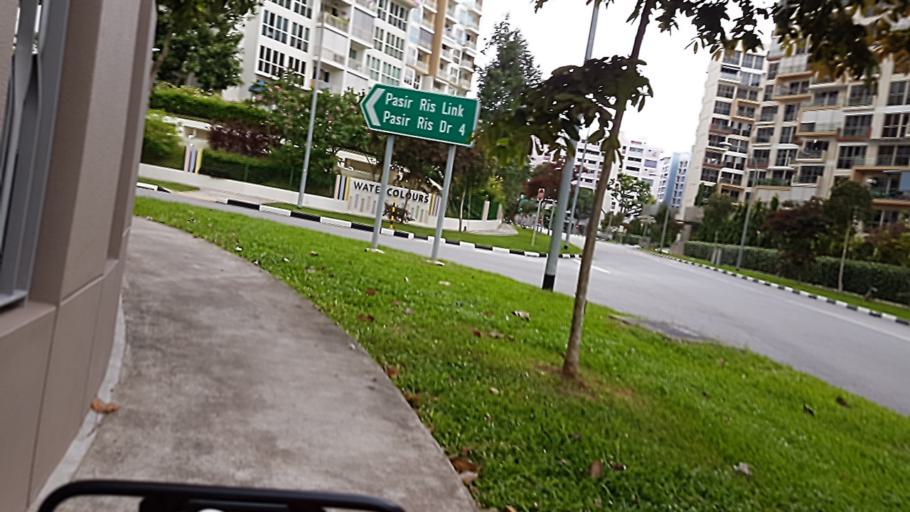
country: MY
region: Johor
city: Kampung Pasir Gudang Baru
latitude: 1.3774
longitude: 103.9592
